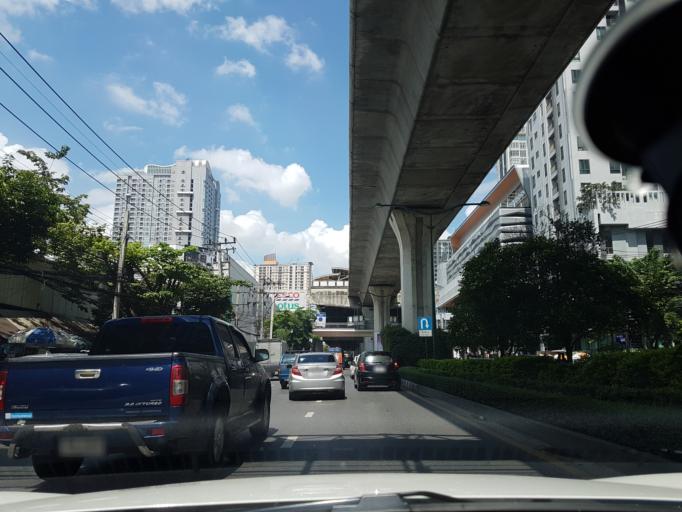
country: TH
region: Bangkok
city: Phra Khanong
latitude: 13.7043
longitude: 100.6016
